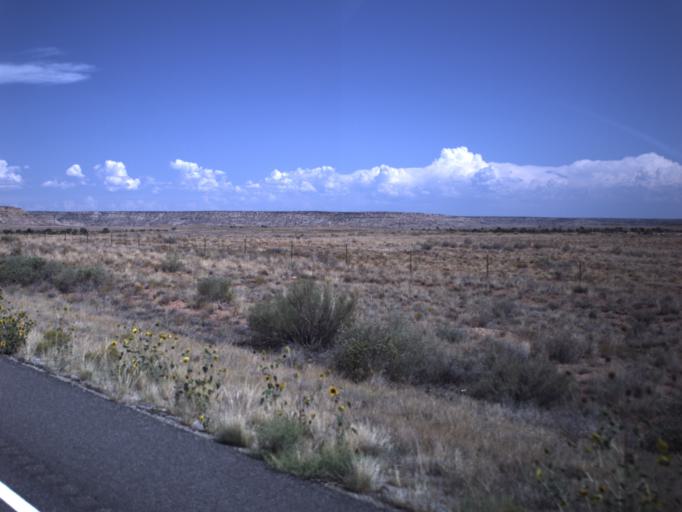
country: US
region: Utah
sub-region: San Juan County
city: Blanding
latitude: 37.4051
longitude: -109.4908
